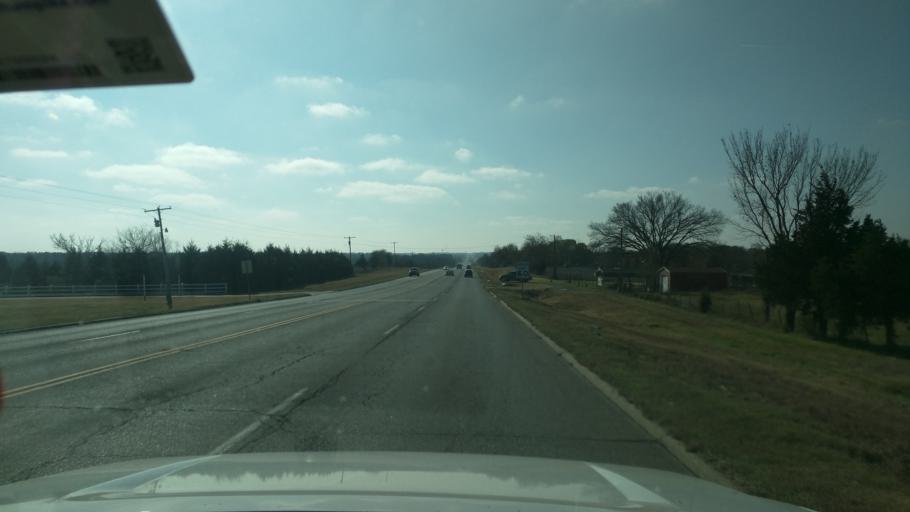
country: US
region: Oklahoma
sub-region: Washington County
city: Bartlesville
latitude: 36.6817
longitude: -95.9352
